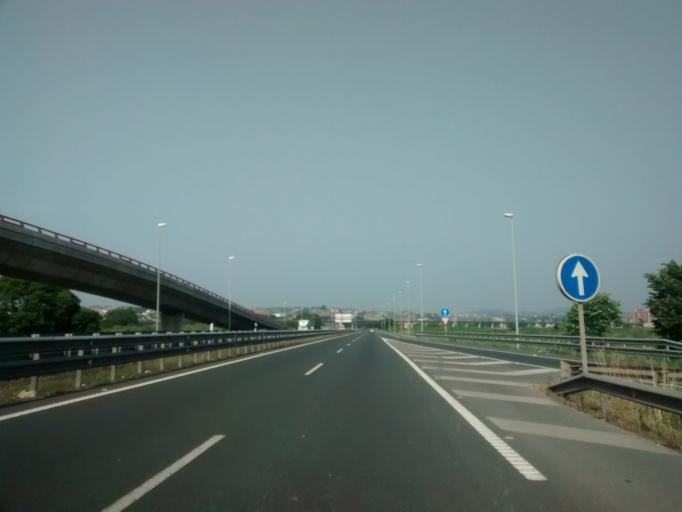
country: ES
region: Cantabria
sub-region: Provincia de Cantabria
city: El Astillero
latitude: 43.4358
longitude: -3.8411
